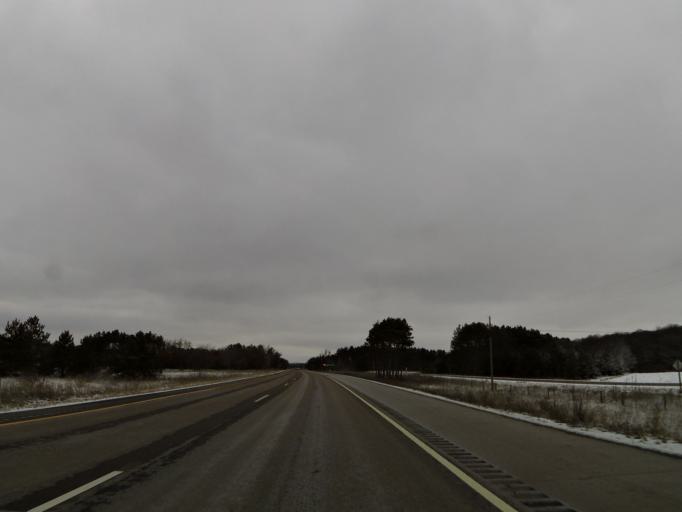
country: US
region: Wisconsin
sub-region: Trempealeau County
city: Osseo
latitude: 44.5484
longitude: -91.1634
